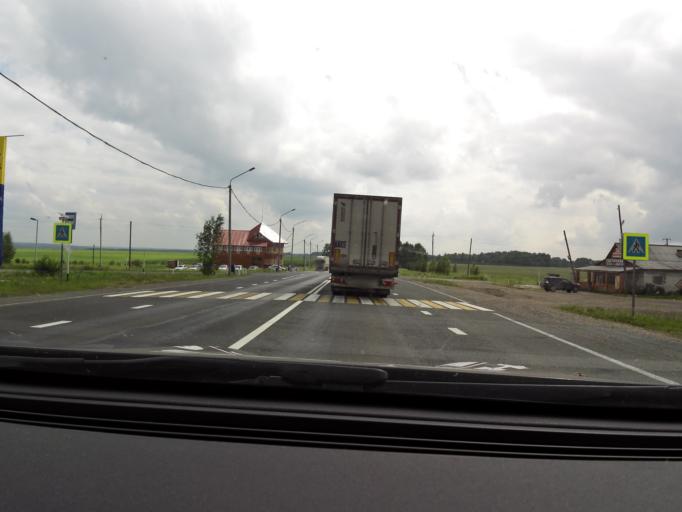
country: RU
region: Perm
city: Suksun
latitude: 56.9538
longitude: 57.5262
